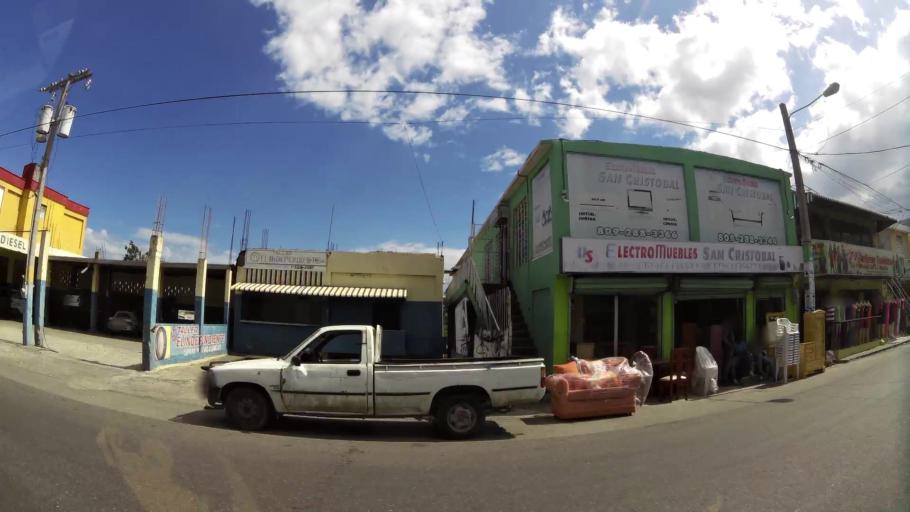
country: DO
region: San Cristobal
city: San Cristobal
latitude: 18.4201
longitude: -70.1012
